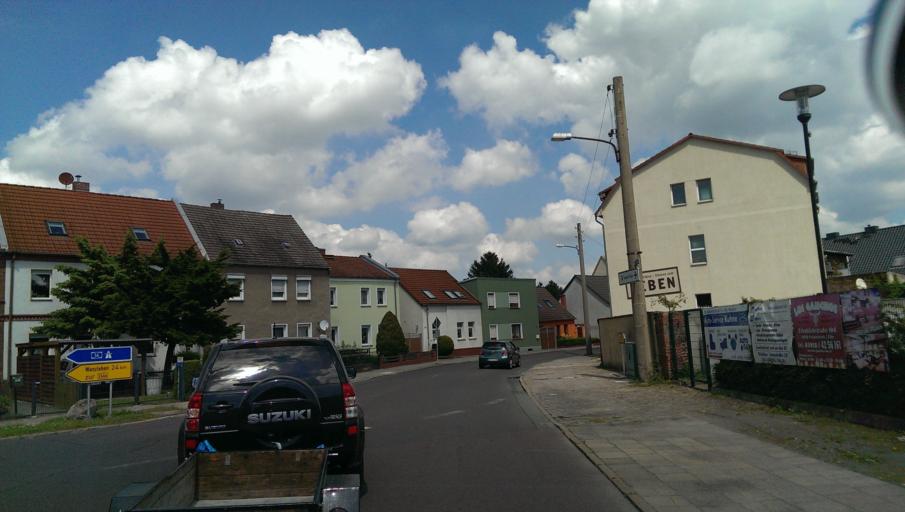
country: DE
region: Saxony-Anhalt
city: Schonebeck
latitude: 52.0012
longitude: 11.7141
